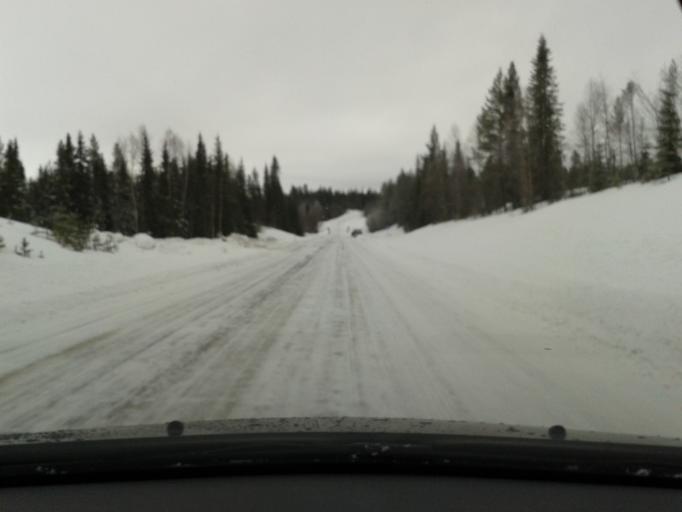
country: SE
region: Vaesterbotten
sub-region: Vilhelmina Kommun
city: Sjoberg
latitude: 64.8242
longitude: 15.9601
